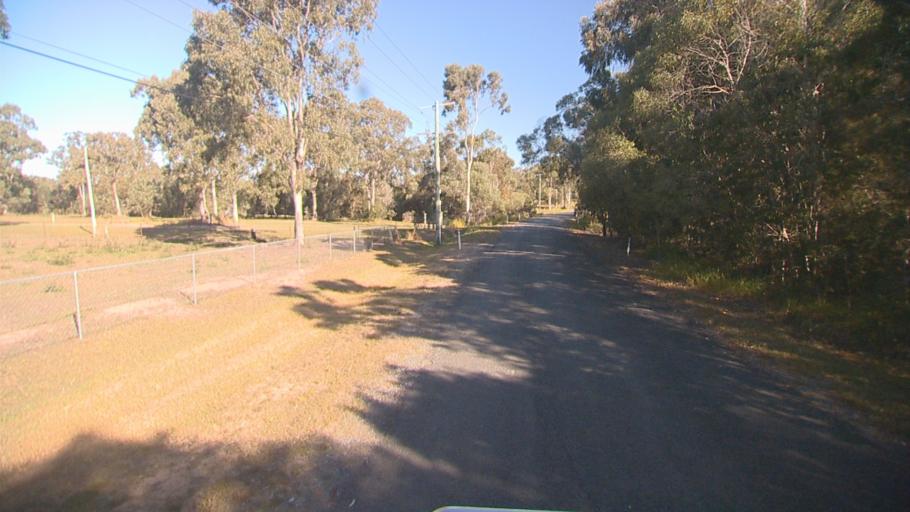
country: AU
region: Queensland
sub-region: Logan
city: Logan Reserve
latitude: -27.7308
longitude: 153.0830
